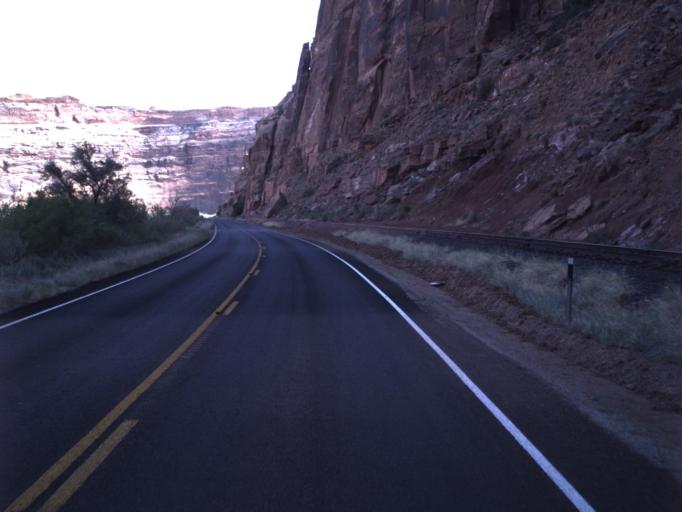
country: US
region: Utah
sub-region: Grand County
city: Moab
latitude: 38.5577
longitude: -109.6559
